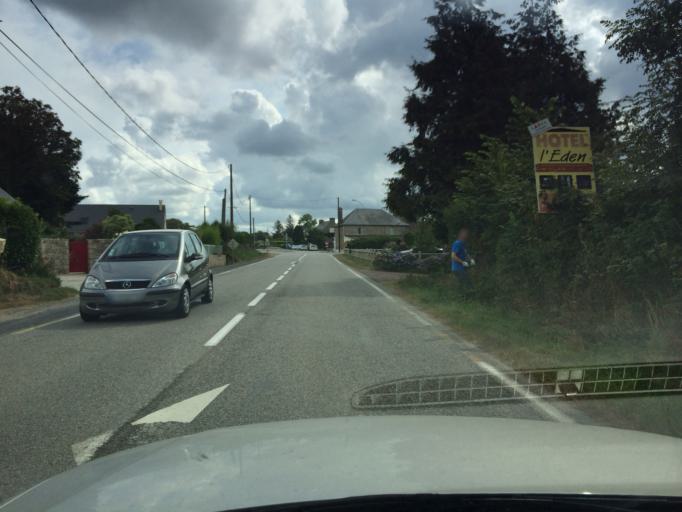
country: FR
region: Lower Normandy
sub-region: Departement de la Manche
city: Brix
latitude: 49.5633
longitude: -1.5934
